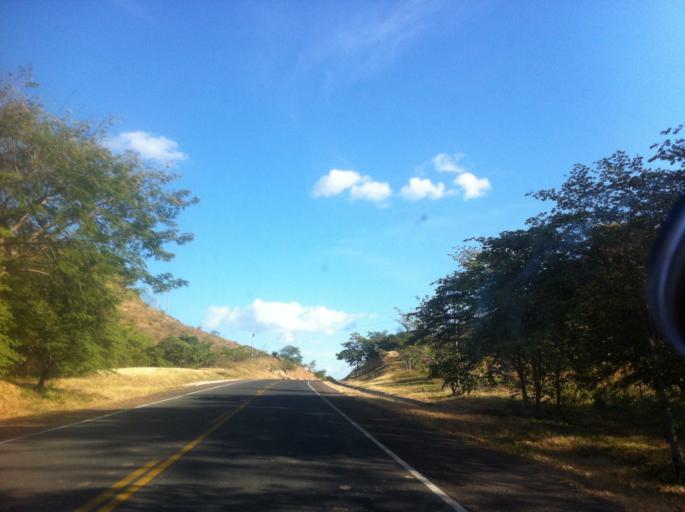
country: NI
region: Chontales
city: Acoyapa
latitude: 11.9478
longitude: -85.1531
